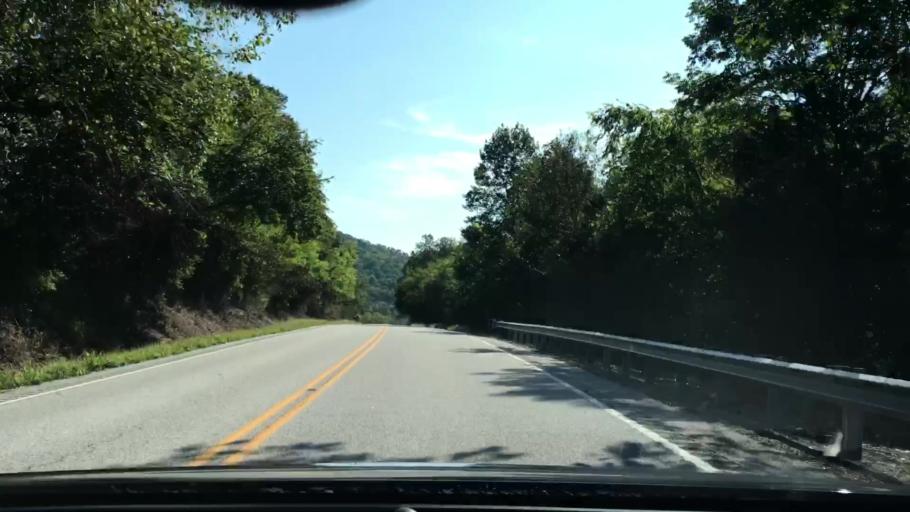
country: US
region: Tennessee
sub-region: Jackson County
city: Gainesboro
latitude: 36.3585
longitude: -85.7417
